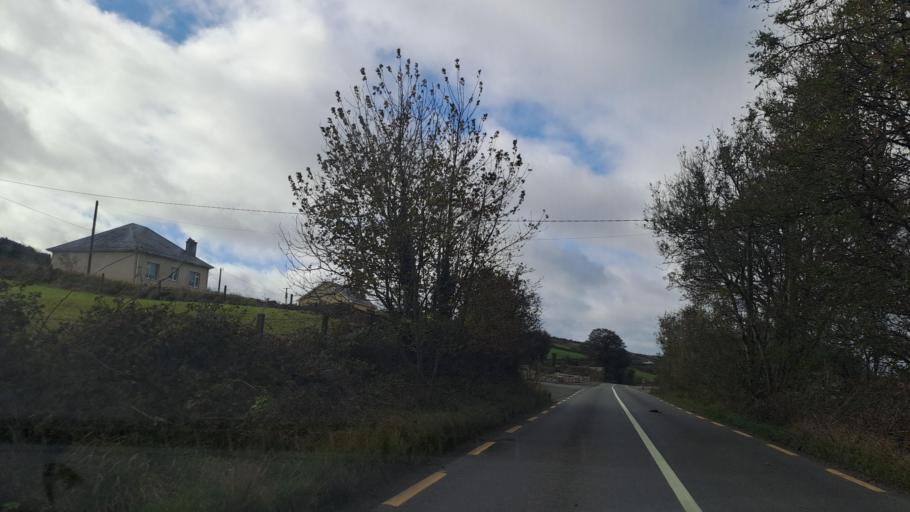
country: IE
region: Ulster
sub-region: An Cabhan
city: Bailieborough
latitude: 53.9324
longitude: -6.8874
